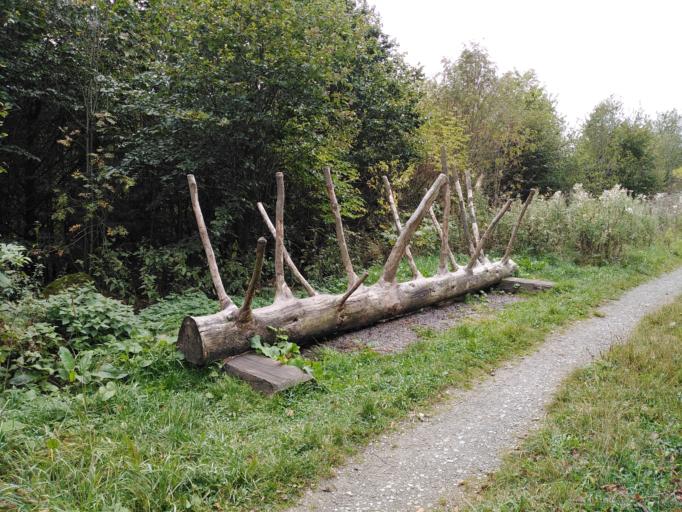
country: DE
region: North Rhine-Westphalia
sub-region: Regierungsbezirk Arnsberg
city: Brilon
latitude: 51.3770
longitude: 8.6039
